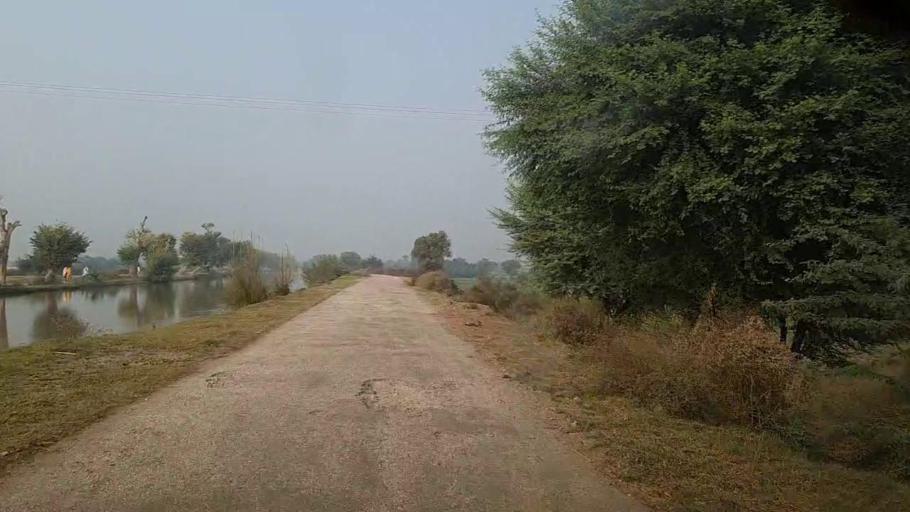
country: PK
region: Sindh
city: Bozdar
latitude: 27.1530
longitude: 68.6604
